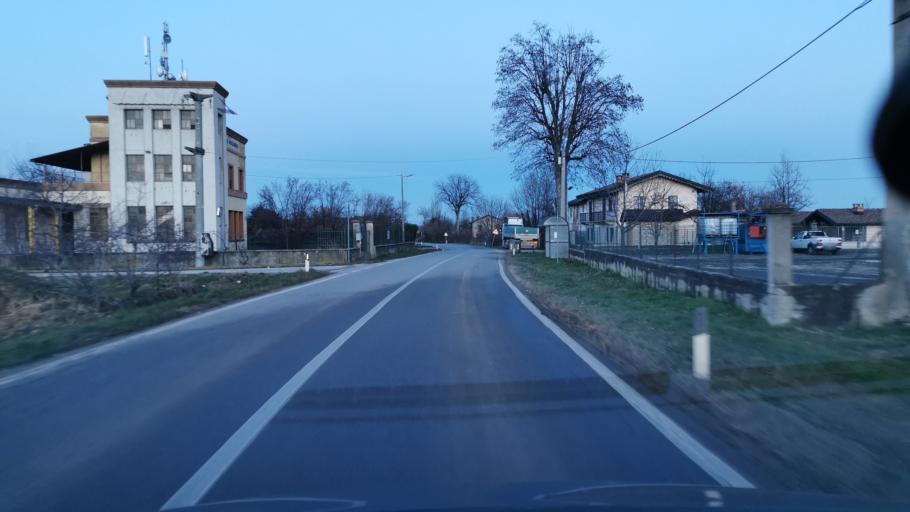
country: IT
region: Piedmont
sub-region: Provincia di Cuneo
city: Caraglio
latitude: 44.4333
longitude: 7.4537
